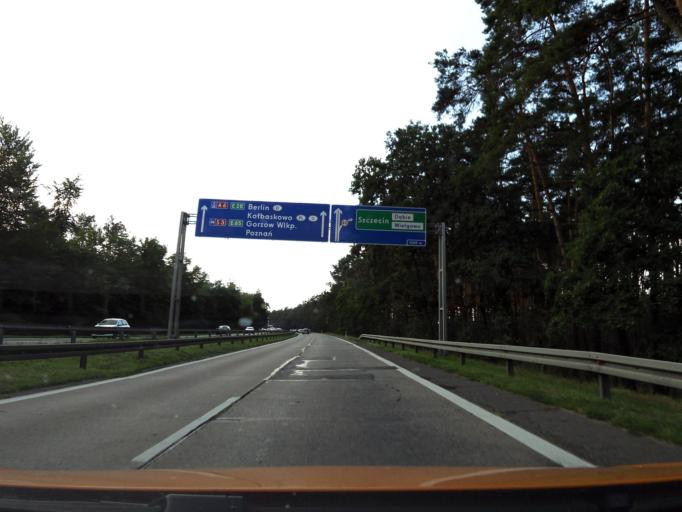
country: PL
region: West Pomeranian Voivodeship
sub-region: Powiat gryfinski
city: Stare Czarnowo
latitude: 53.4107
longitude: 14.7312
